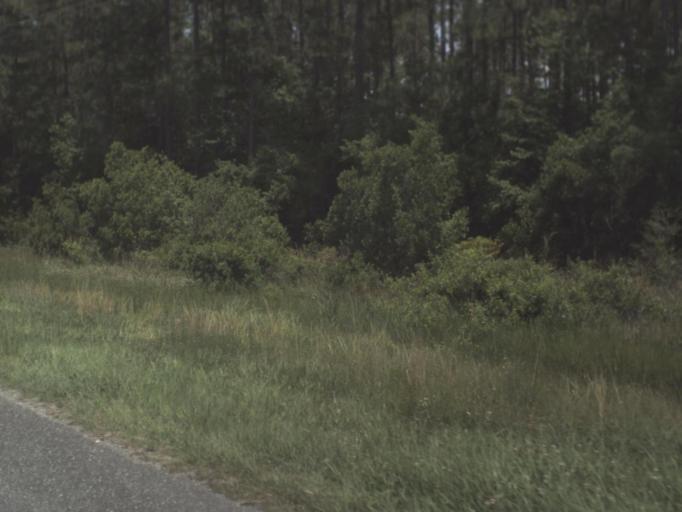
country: US
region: Florida
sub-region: Bradford County
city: Starke
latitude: 29.9622
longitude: -82.1745
